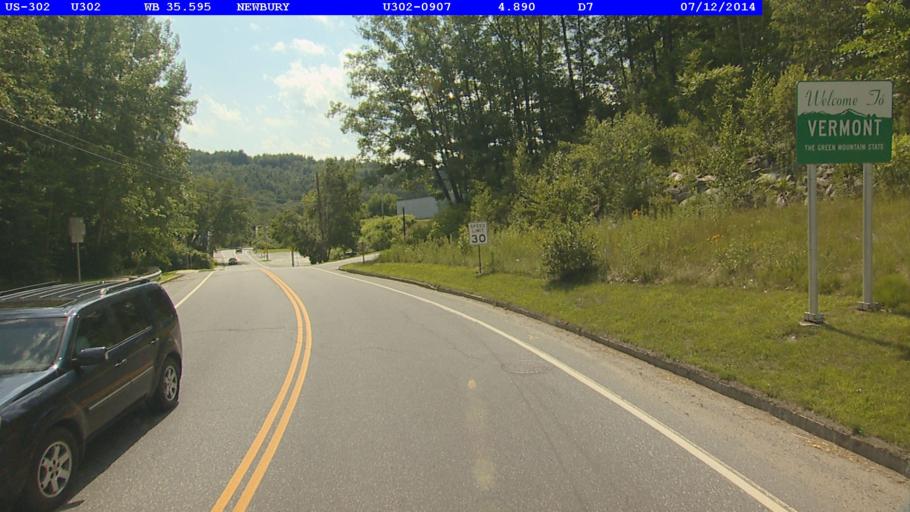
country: US
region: New Hampshire
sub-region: Grafton County
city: Woodsville
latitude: 44.1541
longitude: -72.0418
